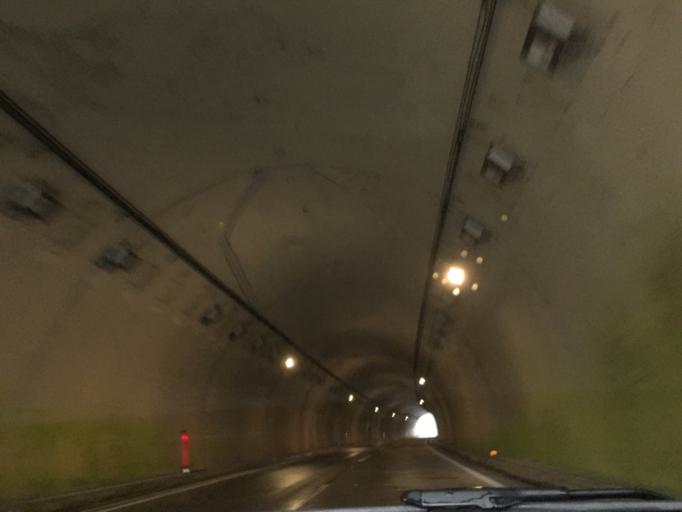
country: JP
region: Tokushima
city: Narutocho-mitsuishi
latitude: 34.2049
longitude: 134.6224
